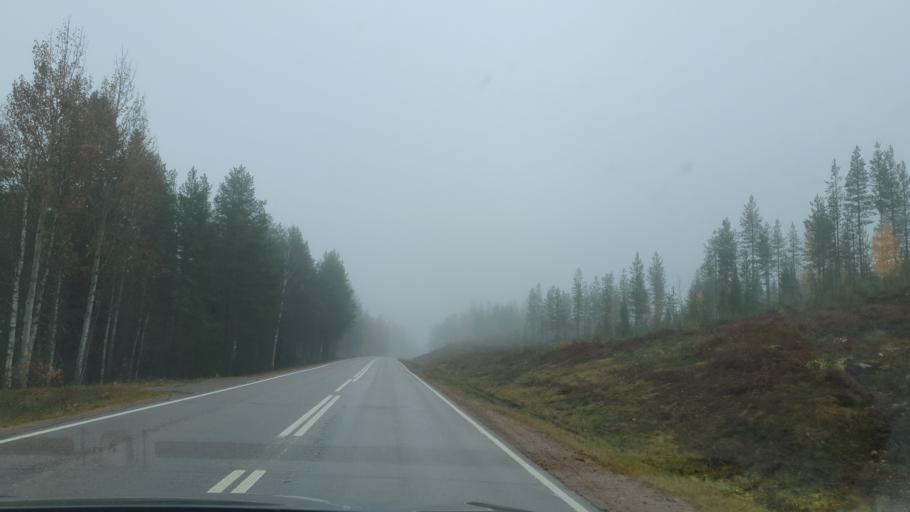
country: FI
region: Lapland
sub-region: Rovaniemi
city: Rovaniemi
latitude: 66.8127
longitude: 25.4020
